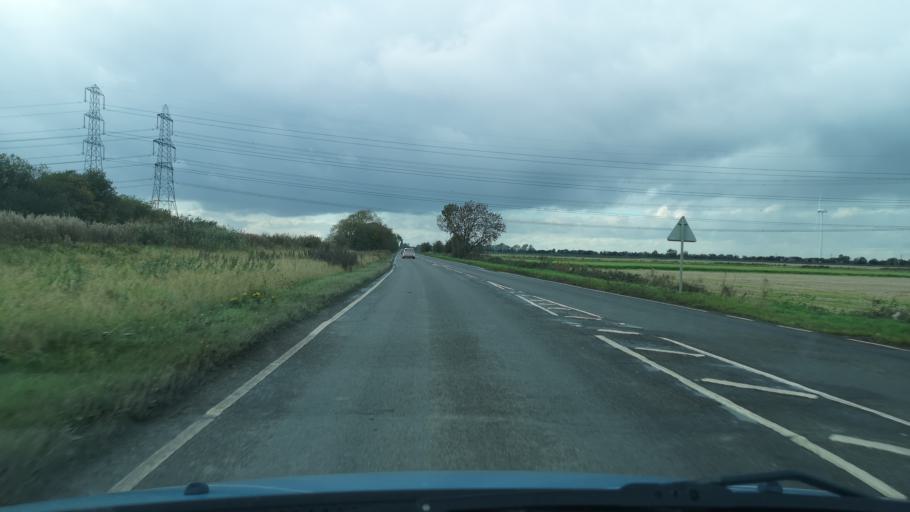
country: GB
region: England
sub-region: North Lincolnshire
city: Gunness
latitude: 53.5769
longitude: -0.7573
